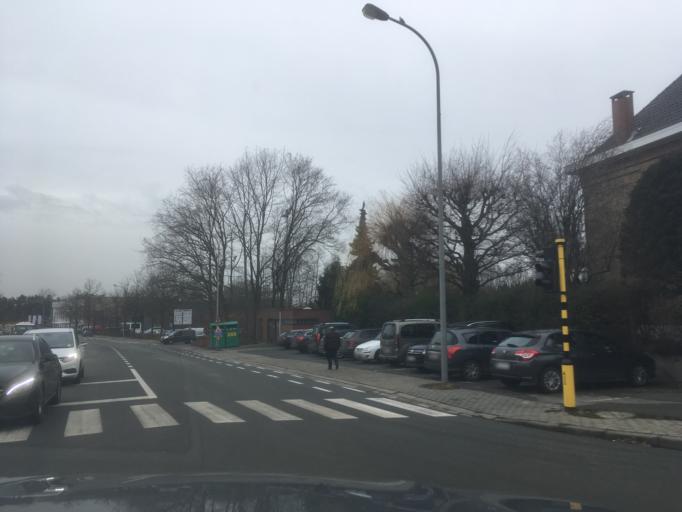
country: BE
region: Flanders
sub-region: Provincie West-Vlaanderen
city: Zwevegem
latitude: 50.8157
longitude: 3.3362
